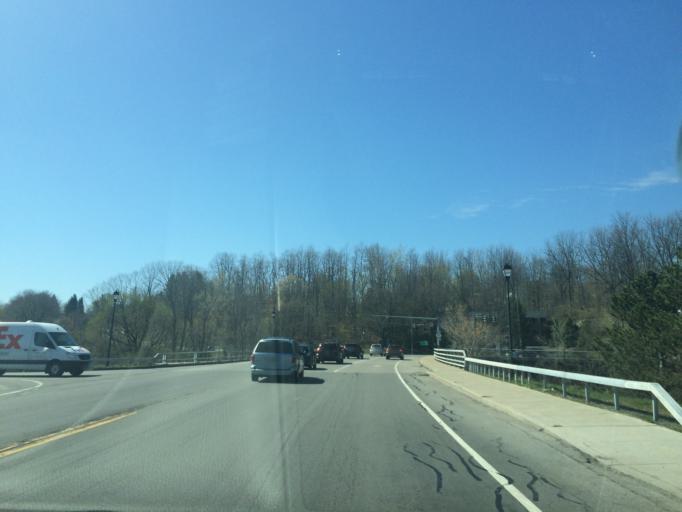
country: US
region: New York
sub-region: Monroe County
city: Fairport
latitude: 43.0978
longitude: -77.4326
